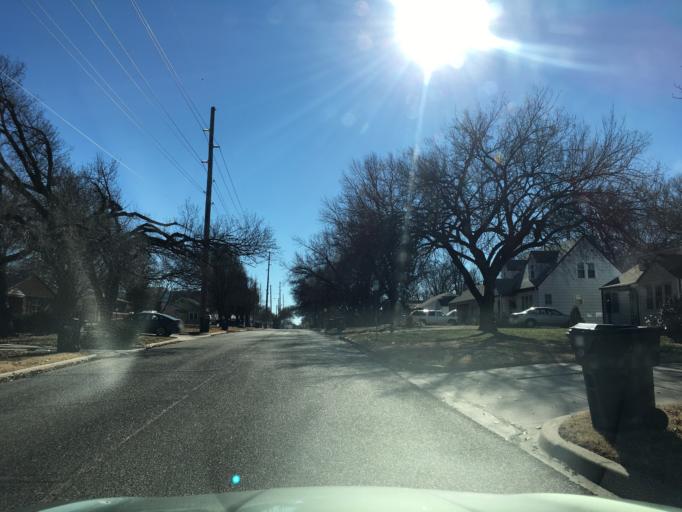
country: US
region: Kansas
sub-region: Sedgwick County
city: Wichita
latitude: 37.6700
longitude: -97.2943
